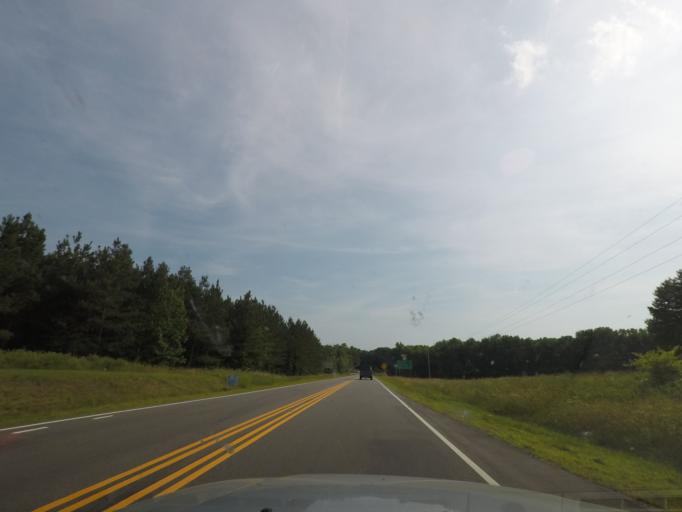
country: US
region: Virginia
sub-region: Mecklenburg County
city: Chase City
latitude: 36.8203
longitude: -78.5966
